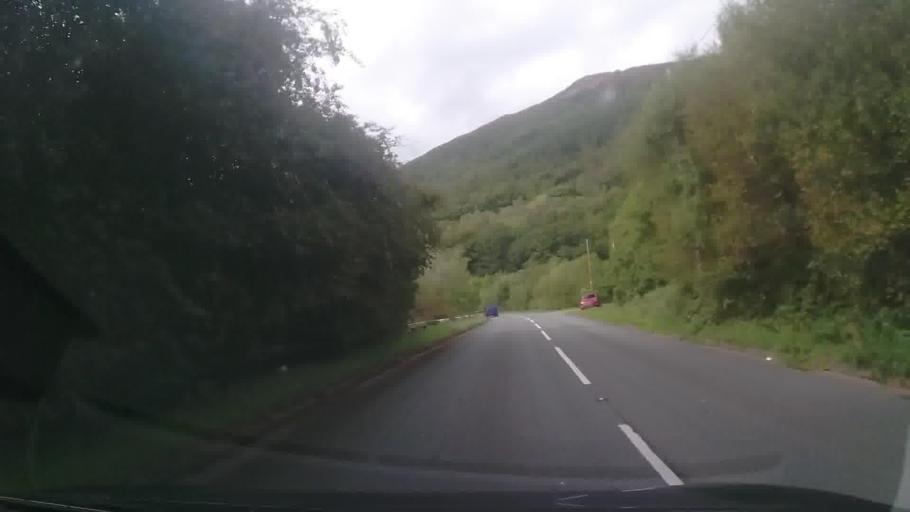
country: GB
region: Wales
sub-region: Gwynedd
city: Dolgellau
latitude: 52.7573
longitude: -3.9161
